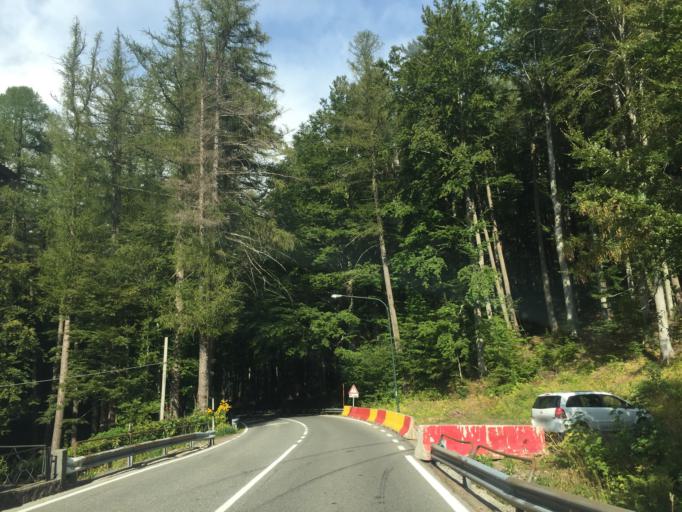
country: IT
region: Tuscany
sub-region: Provincia di Pistoia
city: Abetone
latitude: 44.1250
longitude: 10.7031
